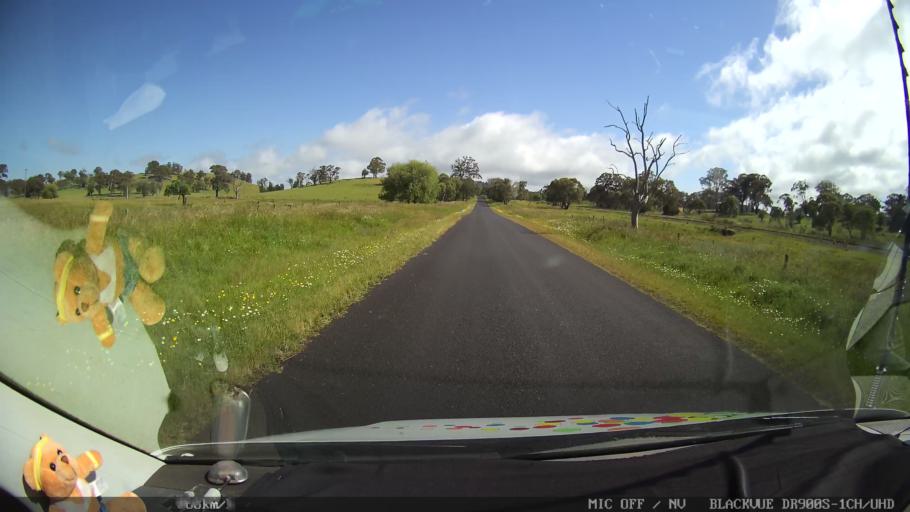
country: AU
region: New South Wales
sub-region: Guyra
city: Guyra
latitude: -30.0436
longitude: 151.6674
